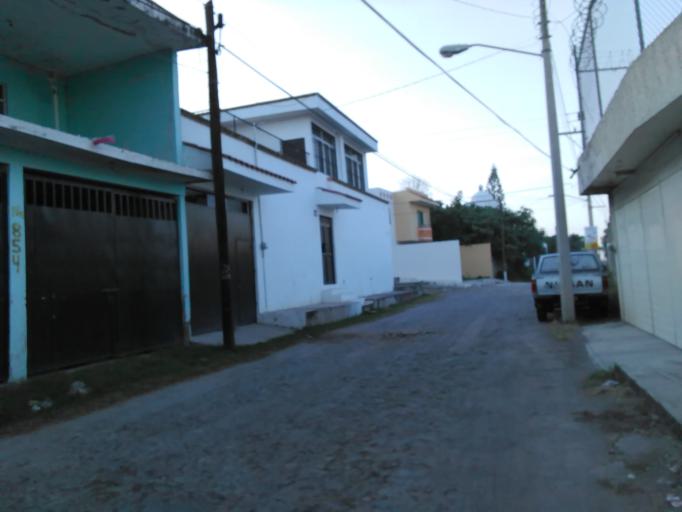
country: MX
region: Nayarit
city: Tepic
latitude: 21.5070
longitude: -104.9200
